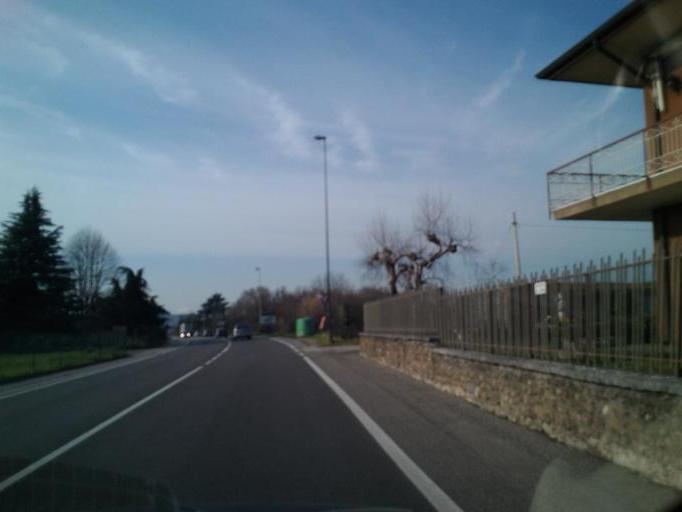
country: IT
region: Veneto
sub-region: Provincia di Verona
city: Mozzecane
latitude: 45.3253
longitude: 10.8324
